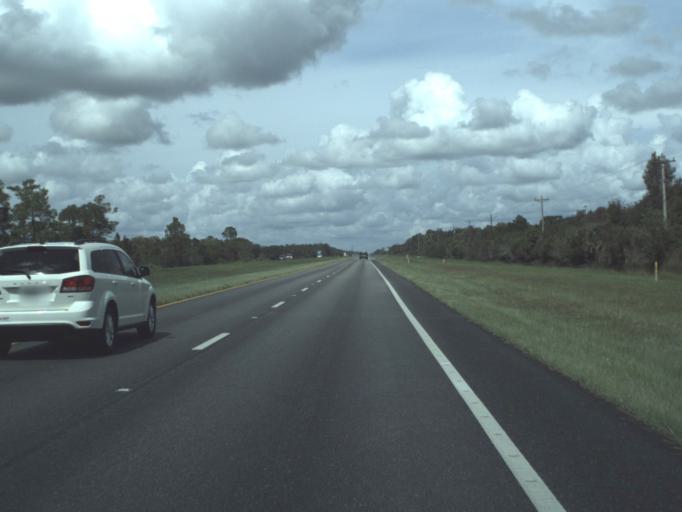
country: US
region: Florida
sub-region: Lee County
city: Suncoast Estates
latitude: 26.7849
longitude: -81.9407
